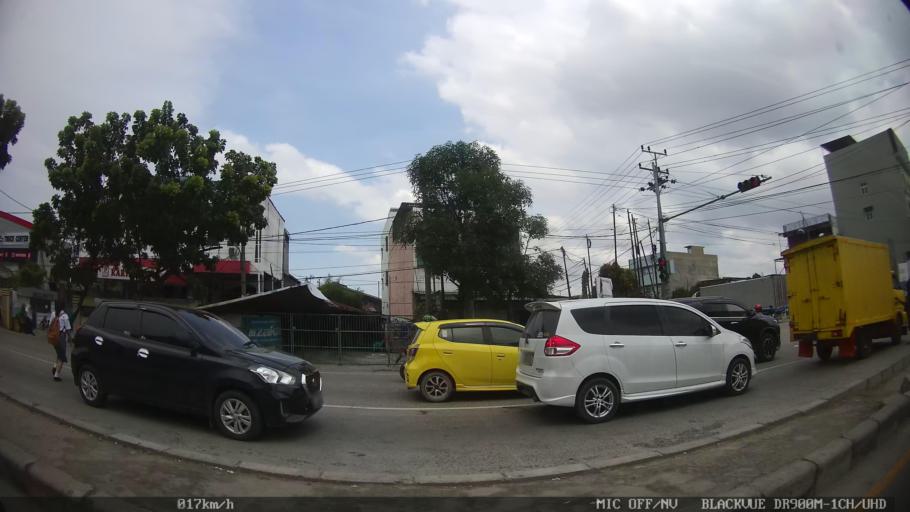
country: ID
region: North Sumatra
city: Medan
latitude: 3.6295
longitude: 98.6815
